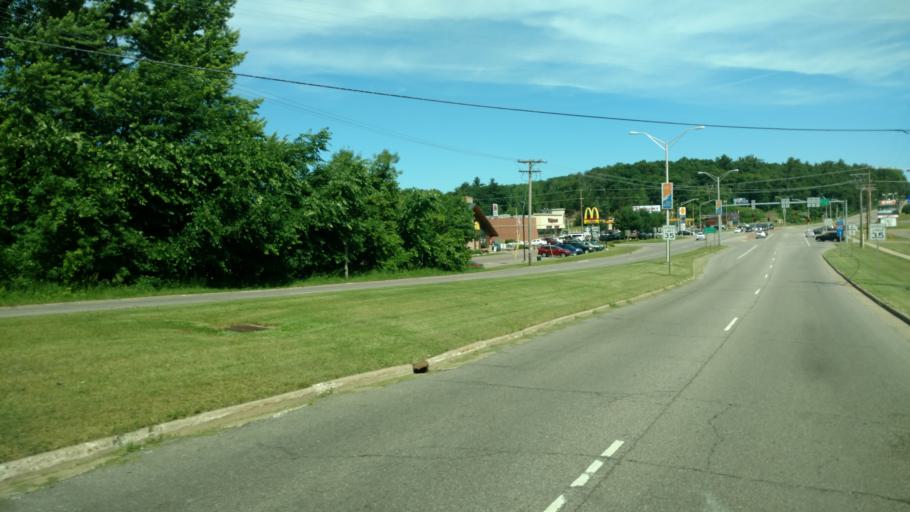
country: US
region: Wisconsin
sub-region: Columbia County
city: Wisconsin Dells
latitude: 43.6238
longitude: -89.7849
